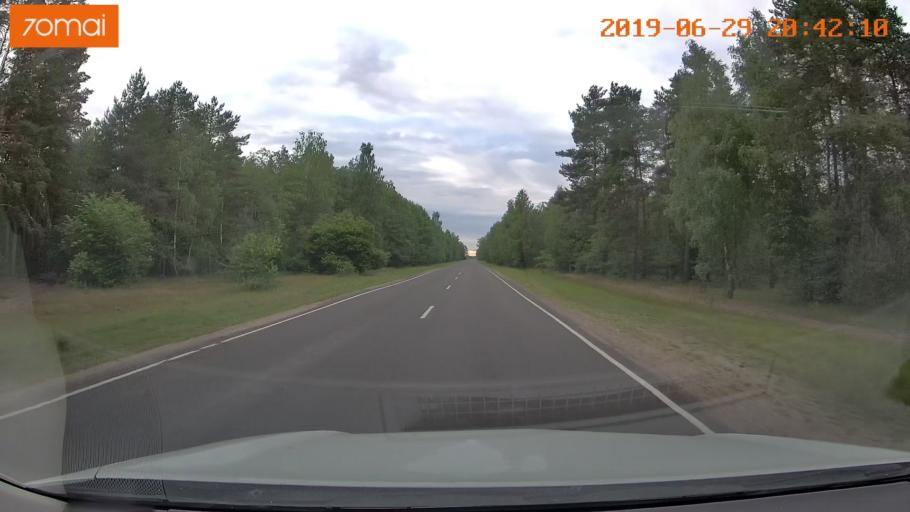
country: BY
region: Brest
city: Hantsavichy
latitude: 52.5944
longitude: 26.3300
